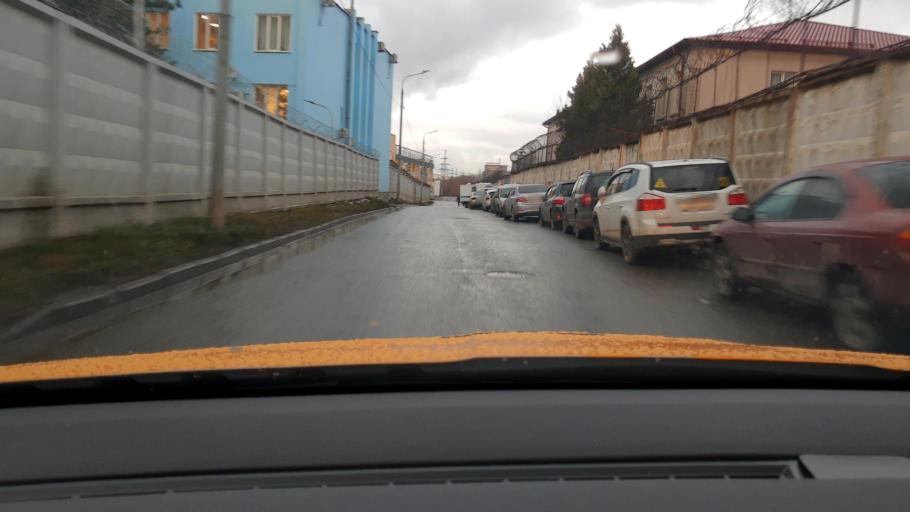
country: RU
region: Moscow
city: Kapotnya
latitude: 55.6602
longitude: 37.8010
